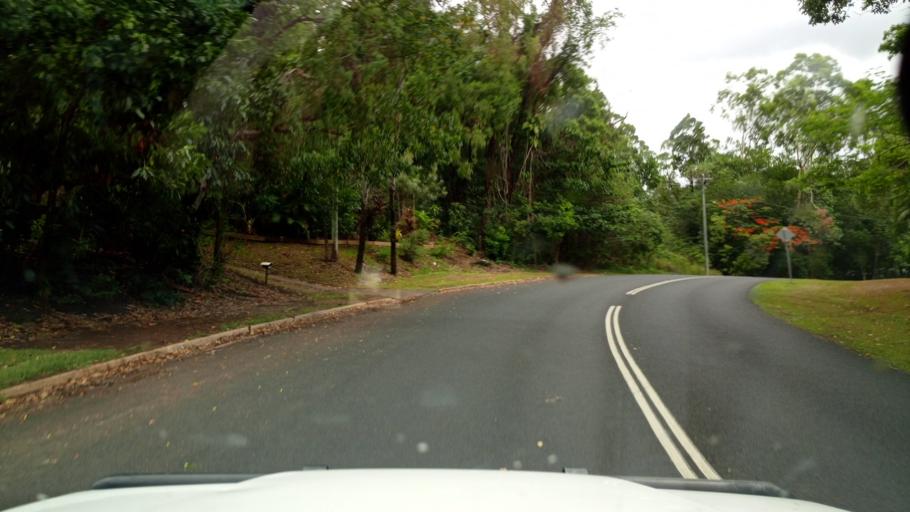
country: AU
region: Queensland
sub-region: Cairns
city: Redlynch
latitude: -16.8830
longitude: 145.7145
